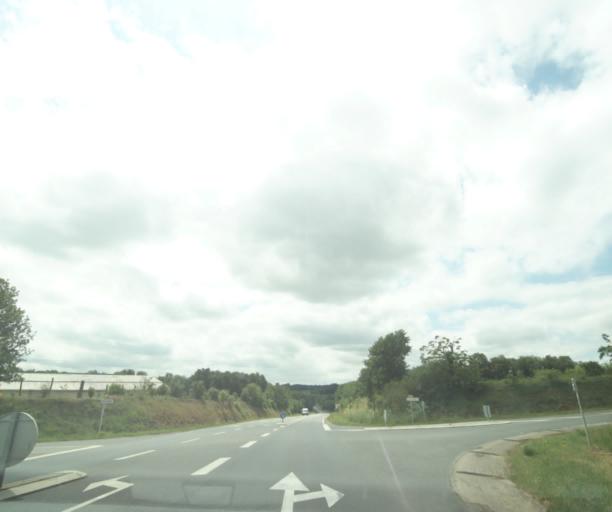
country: FR
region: Poitou-Charentes
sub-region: Departement des Deux-Sevres
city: Saint-Varent
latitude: 46.9193
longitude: -0.1964
